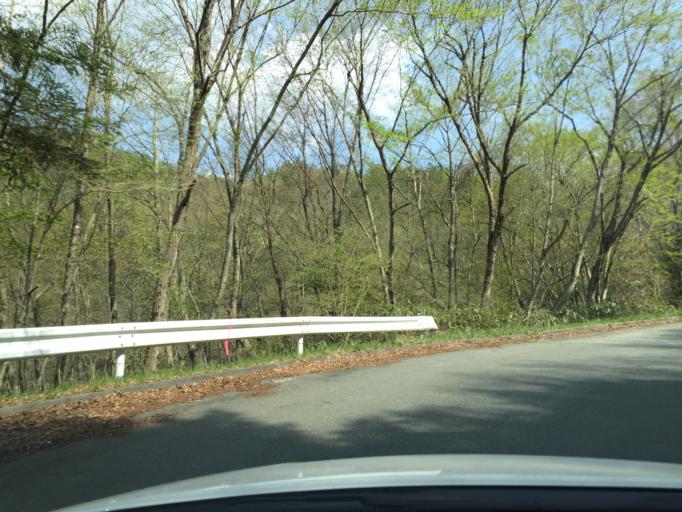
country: JP
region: Fukushima
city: Iwaki
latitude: 37.2631
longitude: 140.8359
